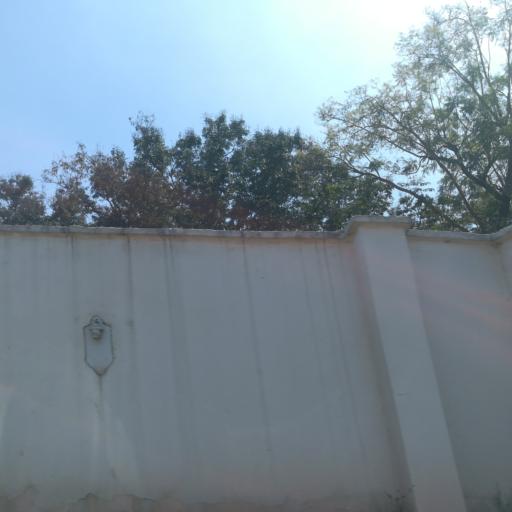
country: NG
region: Plateau
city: Bukuru
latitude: 9.8413
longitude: 8.9014
